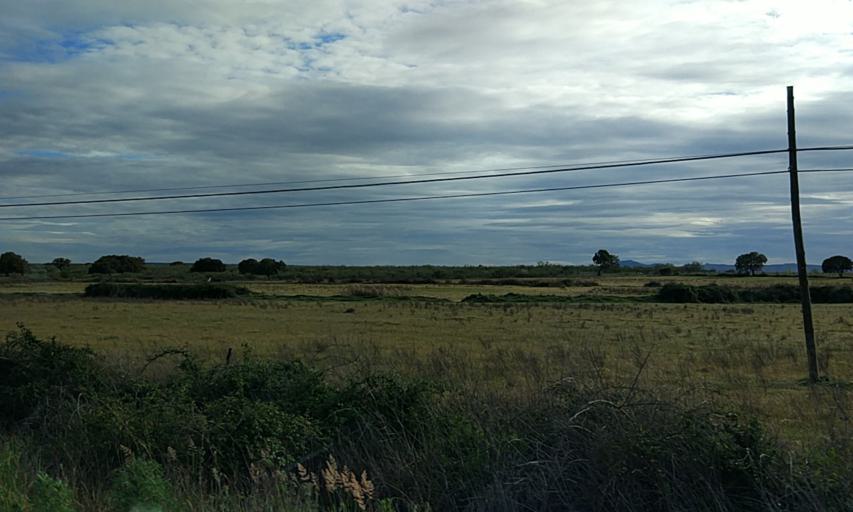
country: ES
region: Extremadura
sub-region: Provincia de Caceres
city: Moraleja
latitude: 40.0550
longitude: -6.6436
